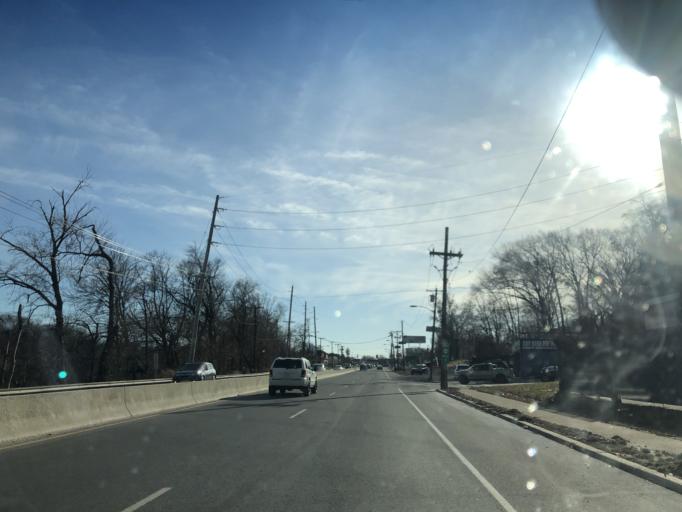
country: US
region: New Jersey
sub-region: Bergen County
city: Fair Lawn
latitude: 40.9285
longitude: -74.1432
